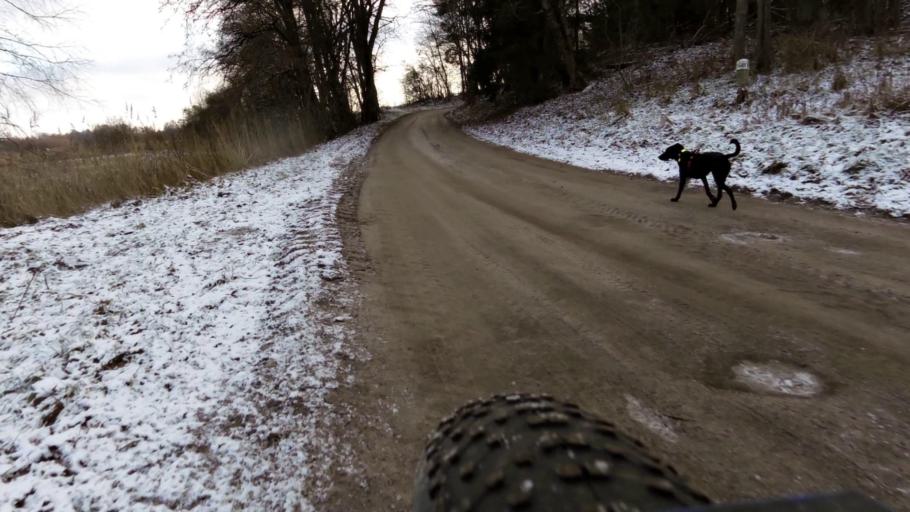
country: PL
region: West Pomeranian Voivodeship
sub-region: Powiat walecki
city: Walcz
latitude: 53.2485
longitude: 16.3725
